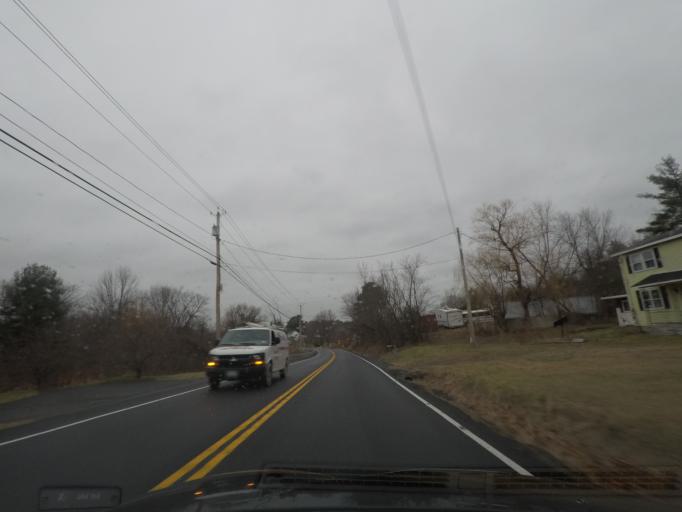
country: US
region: New York
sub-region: Rensselaer County
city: East Greenbush
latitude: 42.6191
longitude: -73.6804
